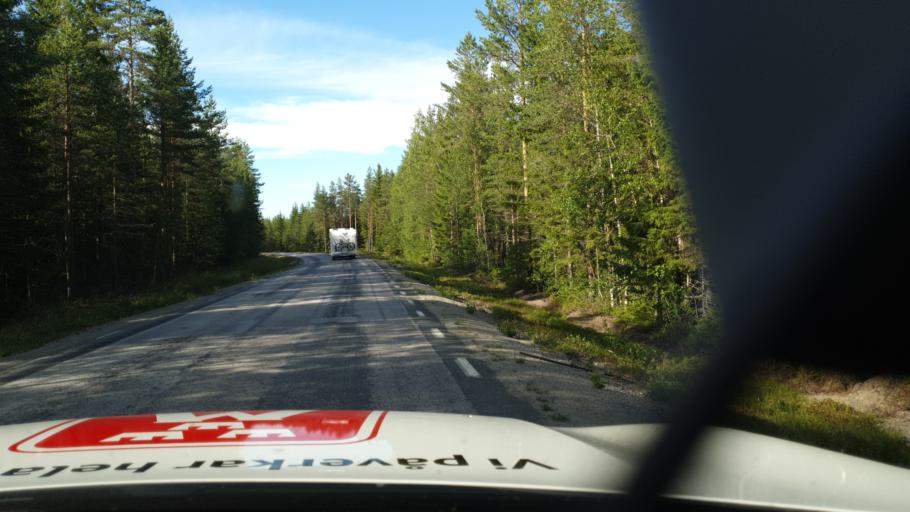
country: SE
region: Vaesterbotten
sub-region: Umea Kommun
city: Saevar
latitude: 63.8734
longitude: 20.5827
